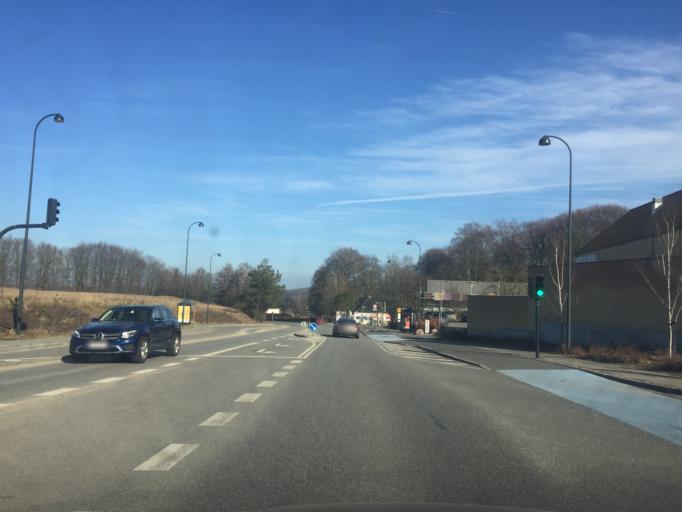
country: DK
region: Capital Region
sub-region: Rudersdal Kommune
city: Trorod
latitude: 55.8335
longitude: 12.5249
